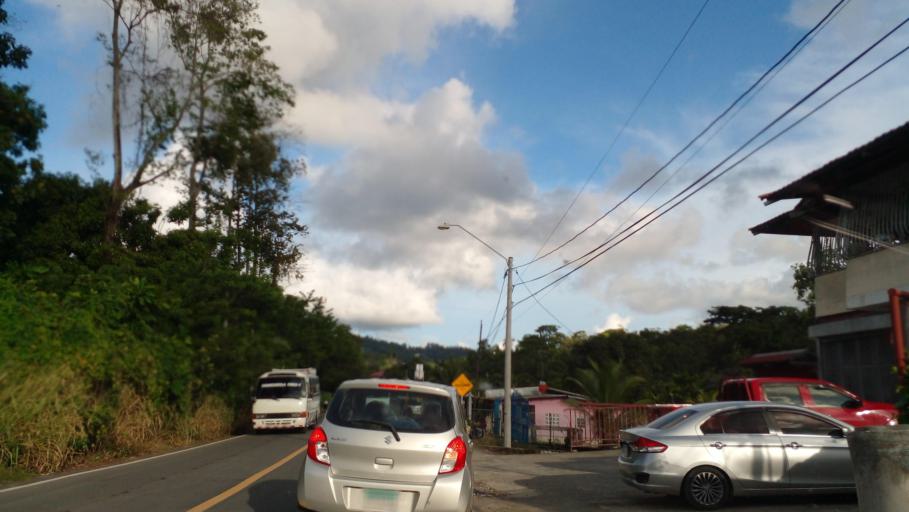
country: PA
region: Bocas del Toro
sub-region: Distrito de Changuinola
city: Changuinola
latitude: 9.4042
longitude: -82.5050
